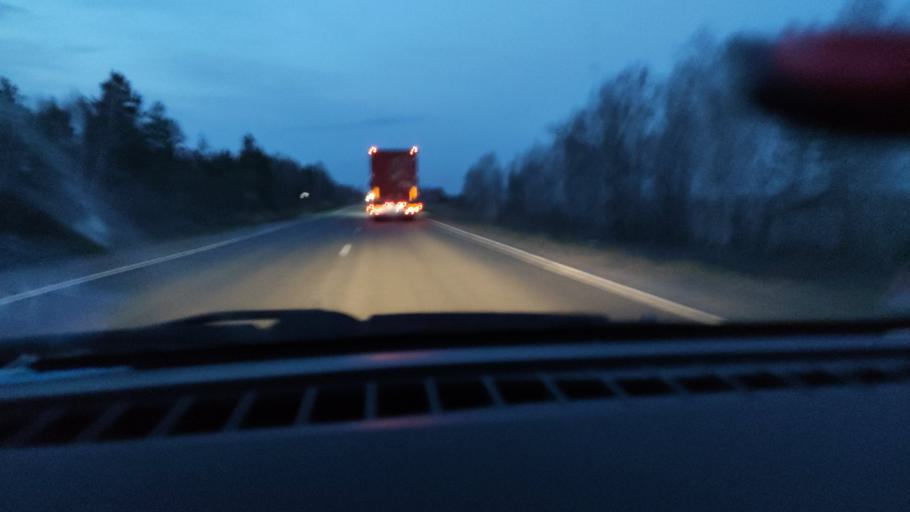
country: RU
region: Saratov
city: Sennoy
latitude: 52.1090
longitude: 46.8267
